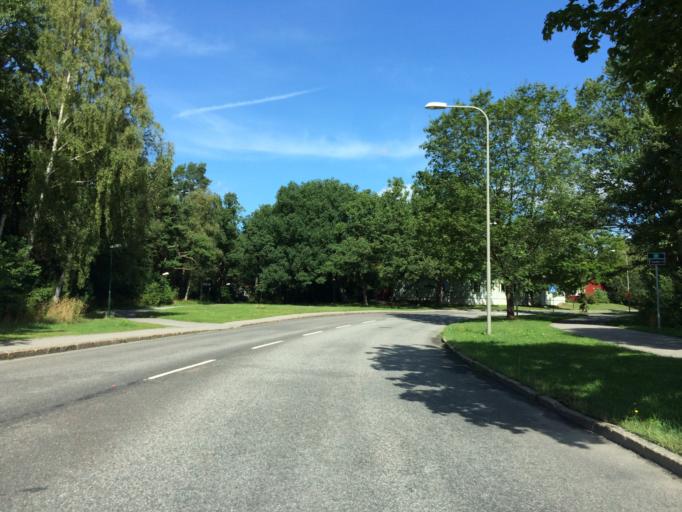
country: SE
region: Stockholm
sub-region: Huddinge Kommun
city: Segeltorp
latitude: 59.2970
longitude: 17.9753
